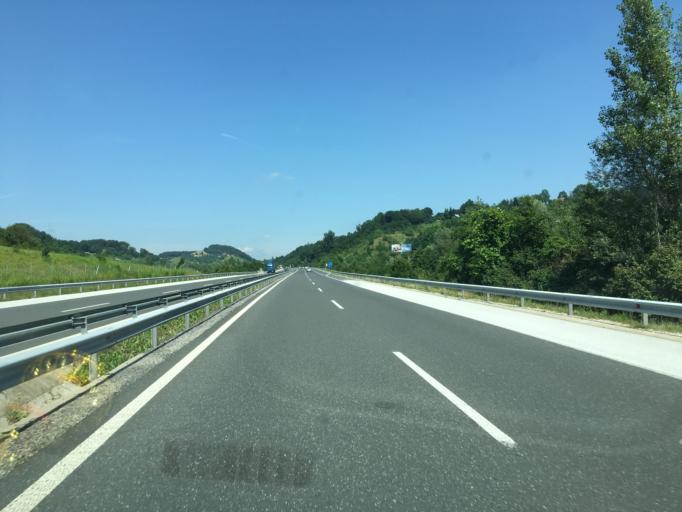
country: SI
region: Sentilj
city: Sentilj v Slov. Goricah
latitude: 46.6495
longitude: 15.6490
